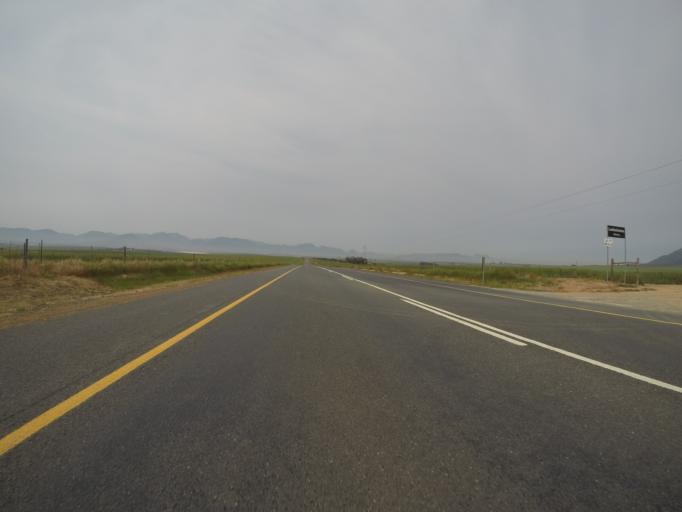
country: ZA
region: Western Cape
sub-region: West Coast District Municipality
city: Malmesbury
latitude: -33.5526
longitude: 18.8708
